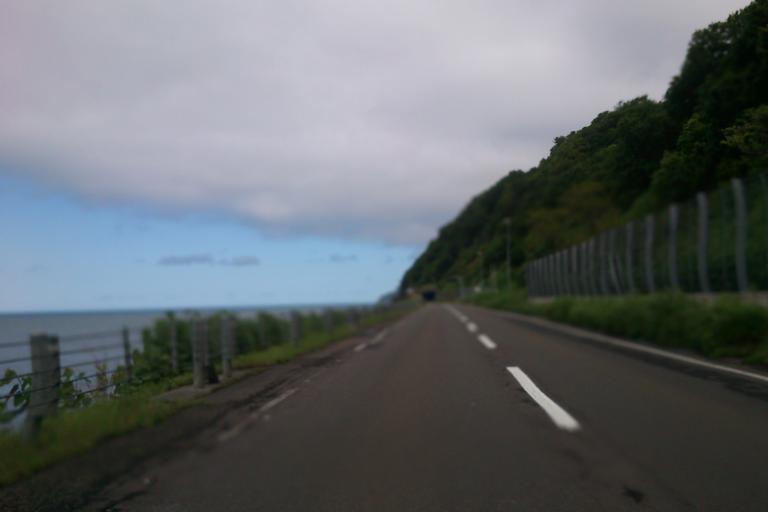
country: JP
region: Hokkaido
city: Ishikari
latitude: 43.4347
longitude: 141.4185
